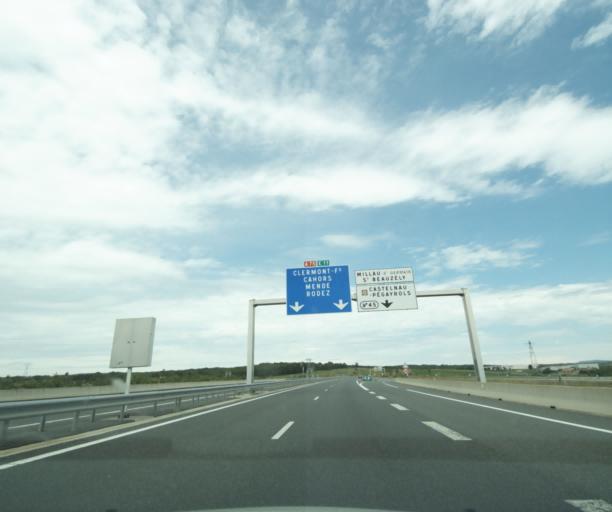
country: FR
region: Midi-Pyrenees
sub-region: Departement de l'Aveyron
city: Creissels
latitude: 44.1370
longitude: 3.0219
